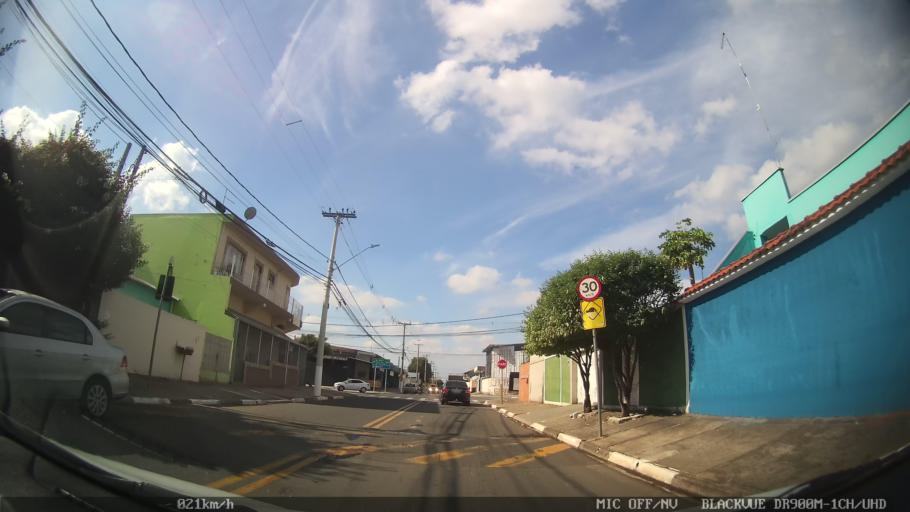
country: BR
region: Sao Paulo
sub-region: Hortolandia
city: Hortolandia
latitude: -22.9072
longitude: -47.2449
